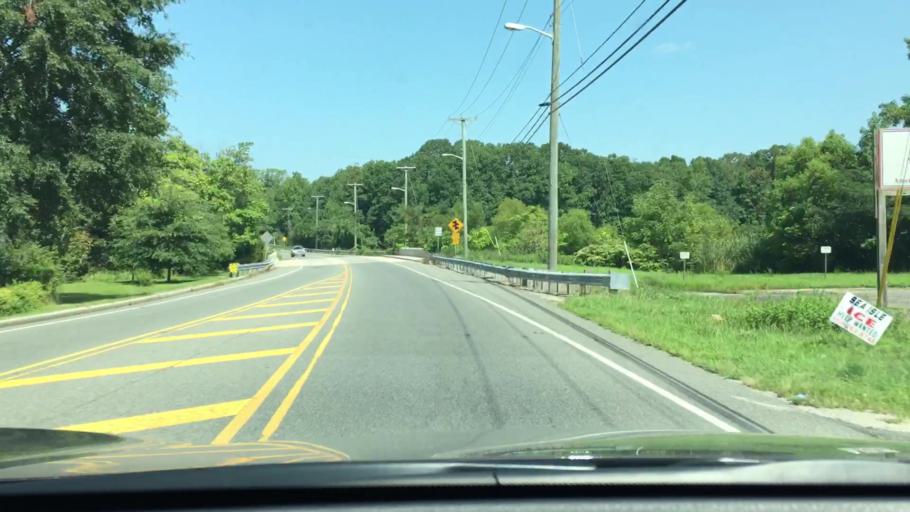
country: US
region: New Jersey
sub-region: Cumberland County
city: Laurel Lake
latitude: 39.3317
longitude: -75.0196
